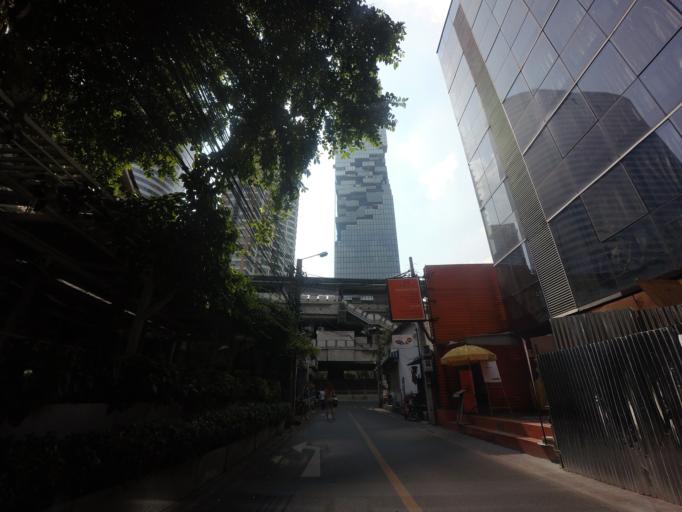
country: TH
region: Bangkok
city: Bang Rak
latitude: 13.7239
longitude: 100.5298
